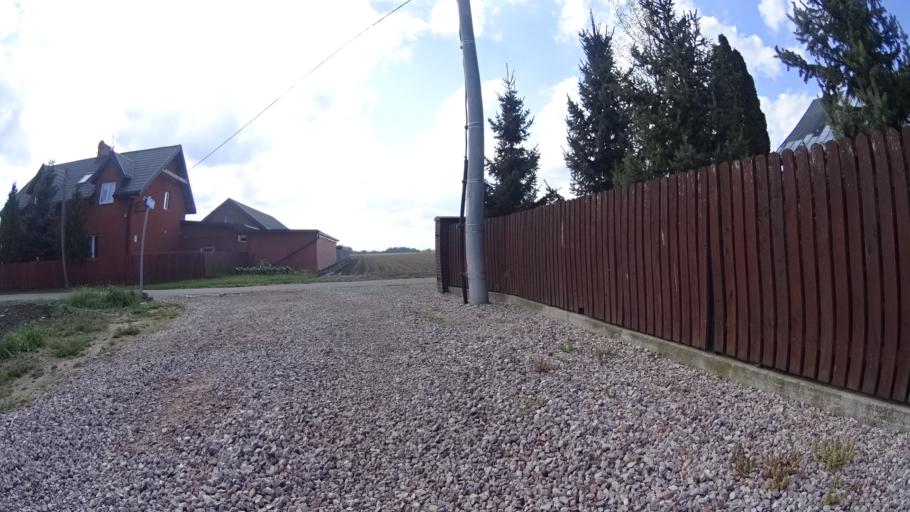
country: PL
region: Masovian Voivodeship
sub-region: Powiat warszawski zachodni
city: Jozefow
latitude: 52.2396
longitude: 20.6739
